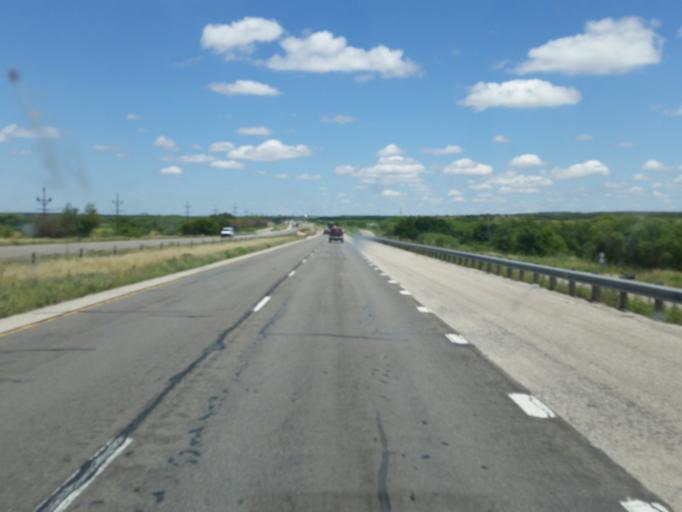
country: US
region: Texas
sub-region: Nolan County
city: Sweetwater
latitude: 32.4943
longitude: -100.2957
